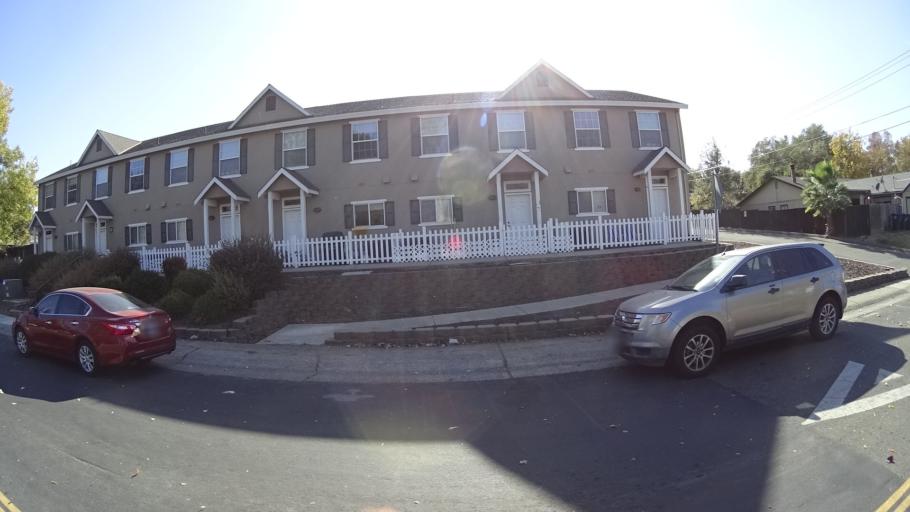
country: US
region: California
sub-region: Sacramento County
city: Citrus Heights
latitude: 38.7020
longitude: -121.2876
